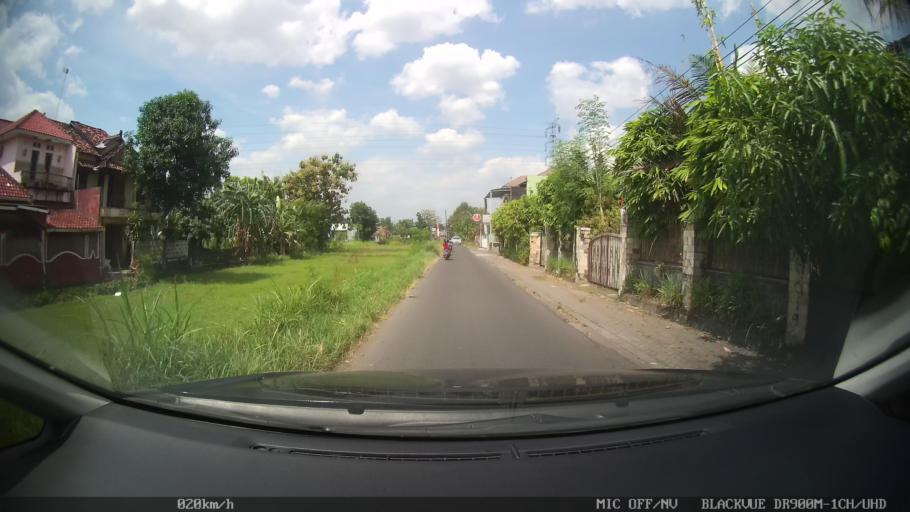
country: ID
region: Daerah Istimewa Yogyakarta
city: Kasihan
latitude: -7.8131
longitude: 110.3406
